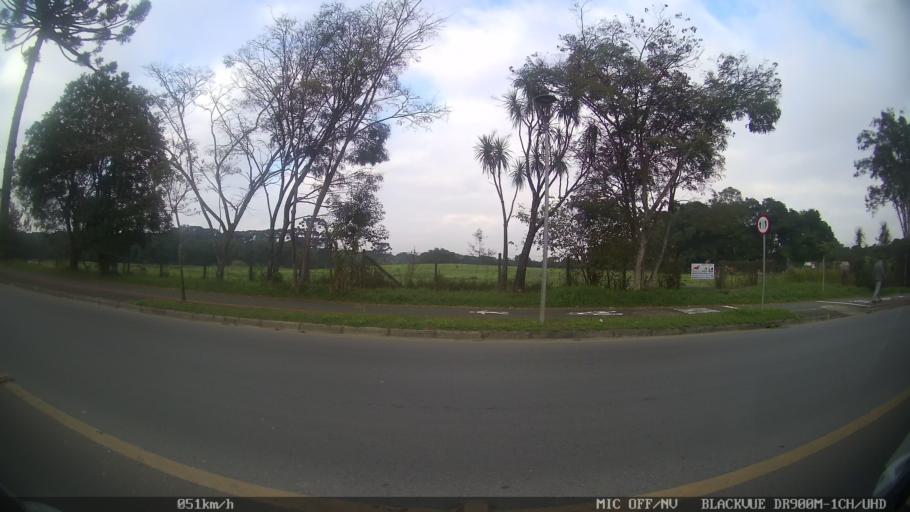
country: BR
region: Parana
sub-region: Almirante Tamandare
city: Almirante Tamandare
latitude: -25.3855
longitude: -49.3243
